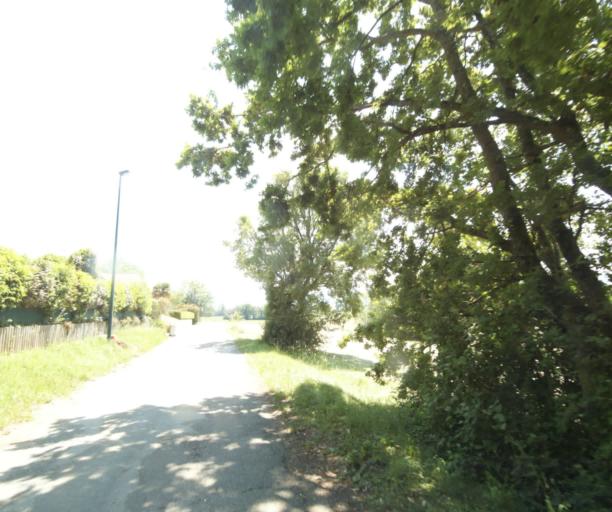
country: FR
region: Rhone-Alpes
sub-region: Departement de la Haute-Savoie
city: Messery
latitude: 46.3646
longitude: 6.3358
